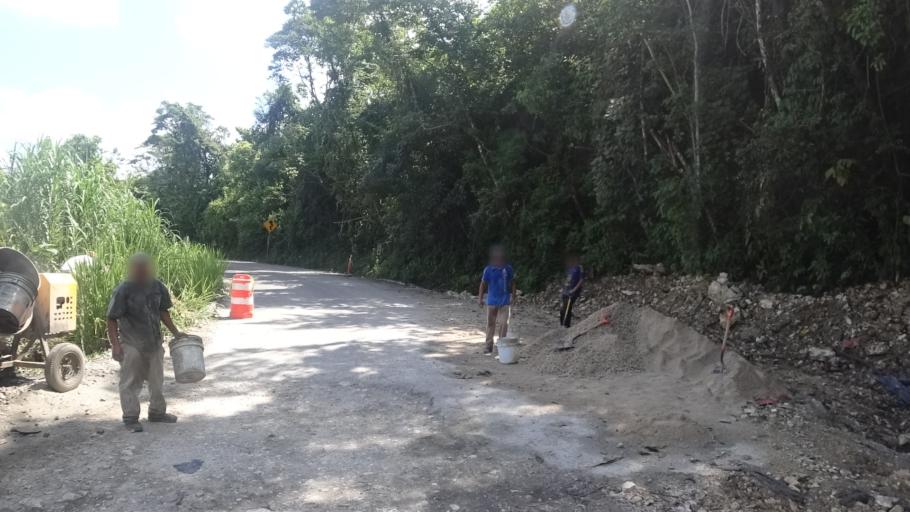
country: MX
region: Chiapas
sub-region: Salto de Agua
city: Belisario Dominguez
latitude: 17.4437
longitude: -91.9738
